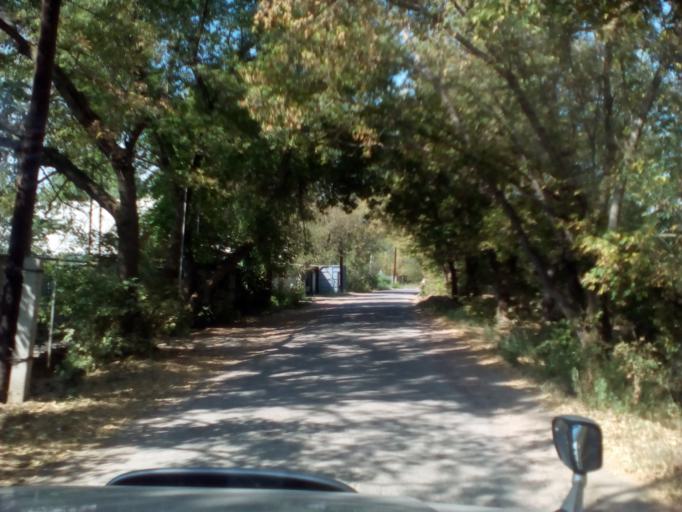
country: KZ
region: Almaty Oblysy
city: Burunday
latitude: 43.1595
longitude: 76.3908
